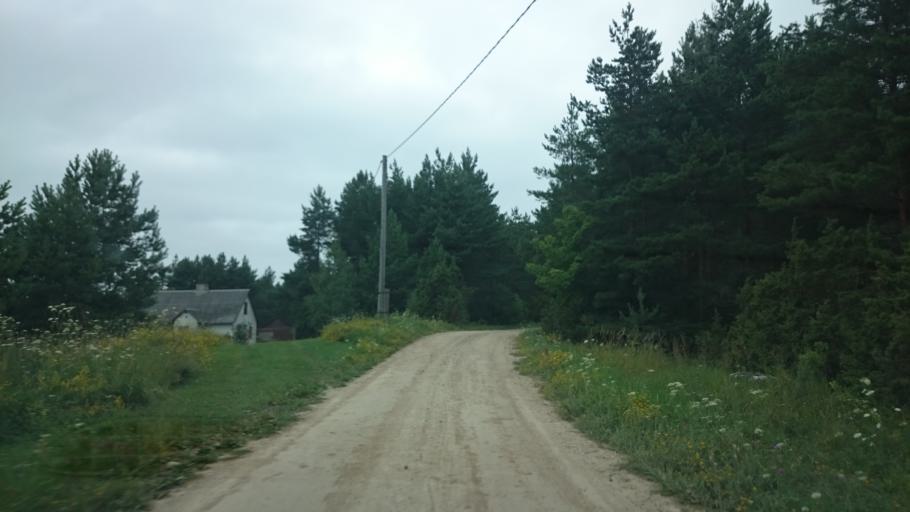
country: EE
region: Saare
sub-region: Orissaare vald
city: Orissaare
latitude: 58.5883
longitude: 22.7052
